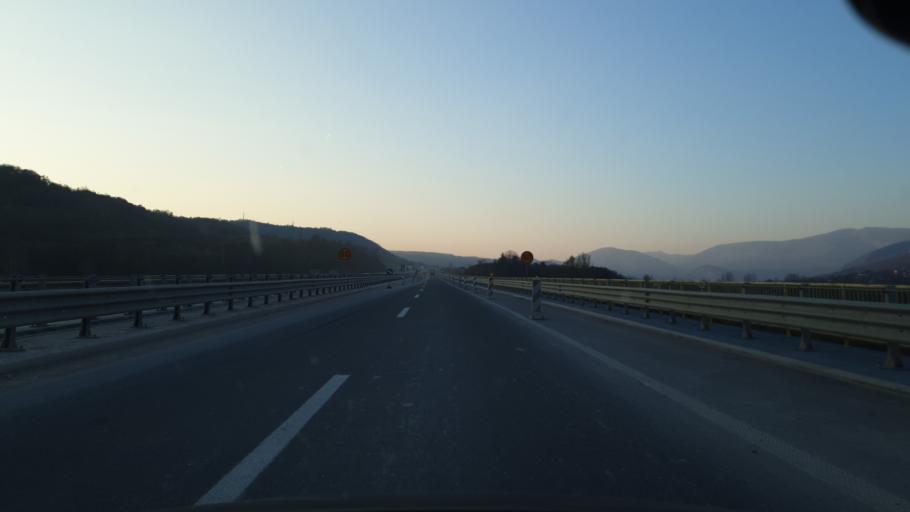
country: RS
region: Central Serbia
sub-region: Pirotski Okrug
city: Bela Palanka
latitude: 43.2585
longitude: 22.2624
